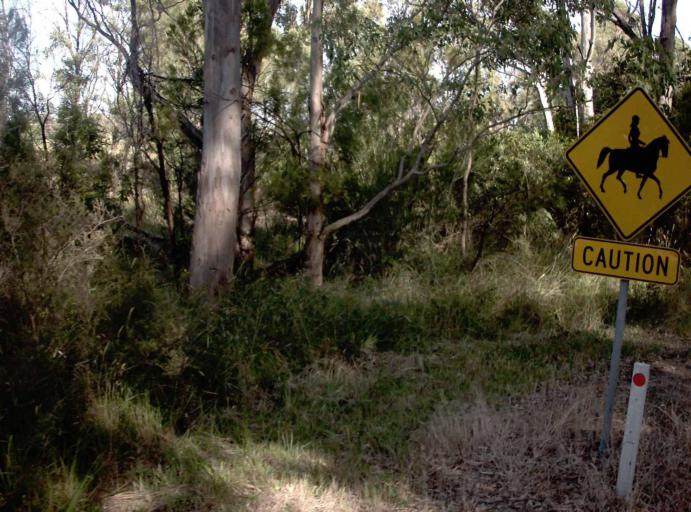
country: AU
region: Victoria
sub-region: East Gippsland
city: Lakes Entrance
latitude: -37.7883
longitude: 147.8295
